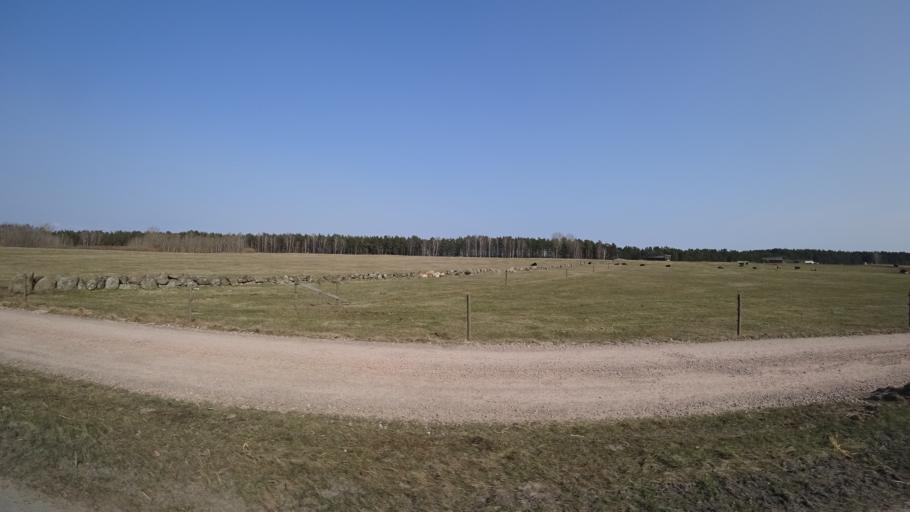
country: SE
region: Skane
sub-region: Kristianstads Kommun
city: Ahus
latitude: 55.9735
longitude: 14.2735
